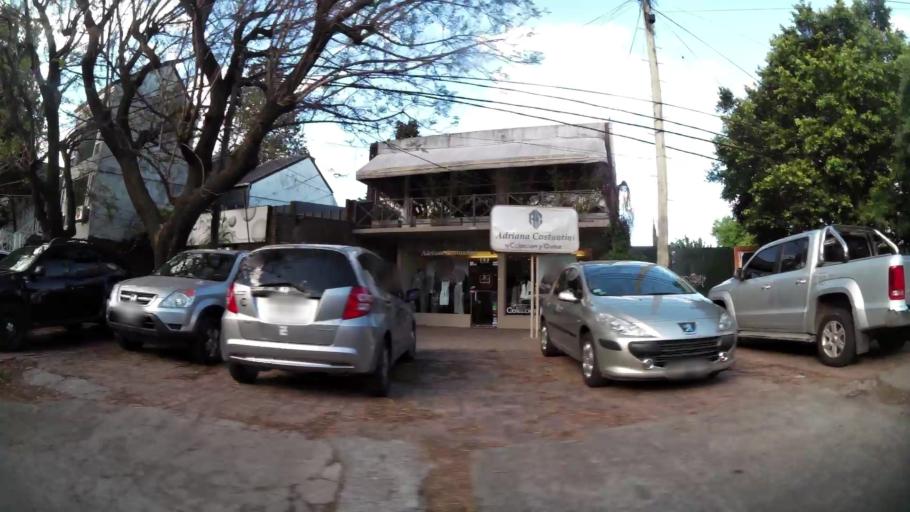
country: AR
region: Buenos Aires
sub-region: Partido de San Isidro
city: San Isidro
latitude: -34.4931
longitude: -58.5528
